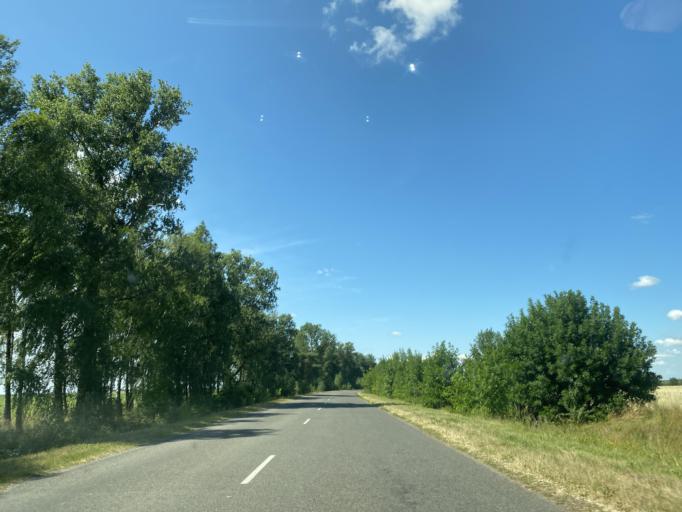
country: BY
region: Brest
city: Ivanava
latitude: 52.1772
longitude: 25.5925
